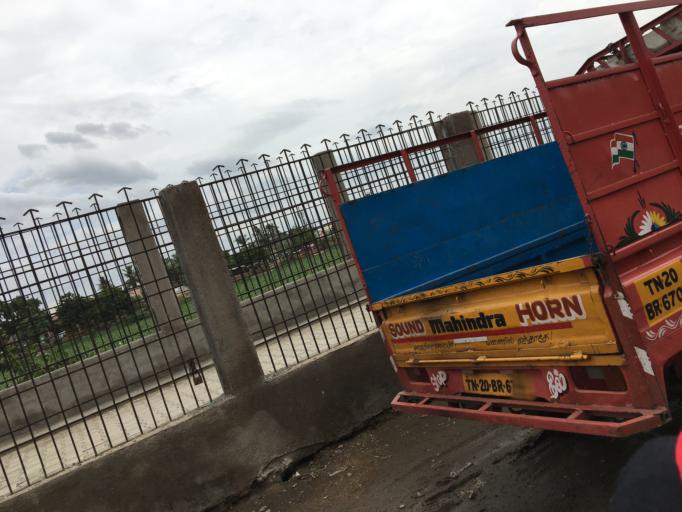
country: IN
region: Tamil Nadu
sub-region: Kancheepuram
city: Alandur
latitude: 12.9879
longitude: 80.2169
